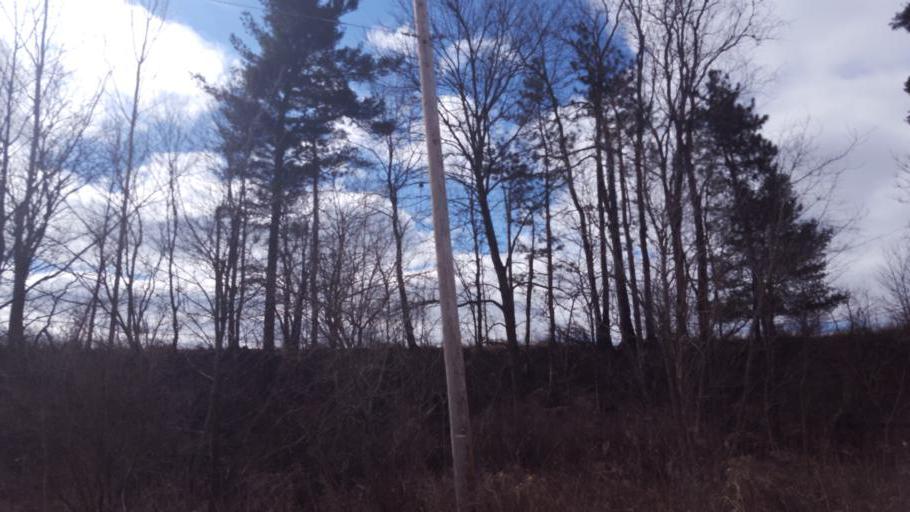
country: US
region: Ohio
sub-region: Sandusky County
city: Bellville
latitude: 40.5561
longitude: -82.5082
